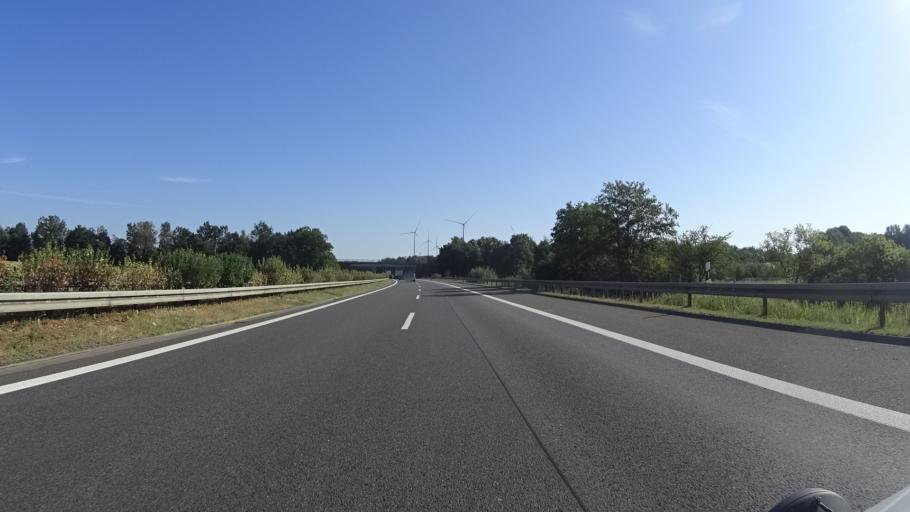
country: DE
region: Brandenburg
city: Grossraschen
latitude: 51.5961
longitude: 13.9513
